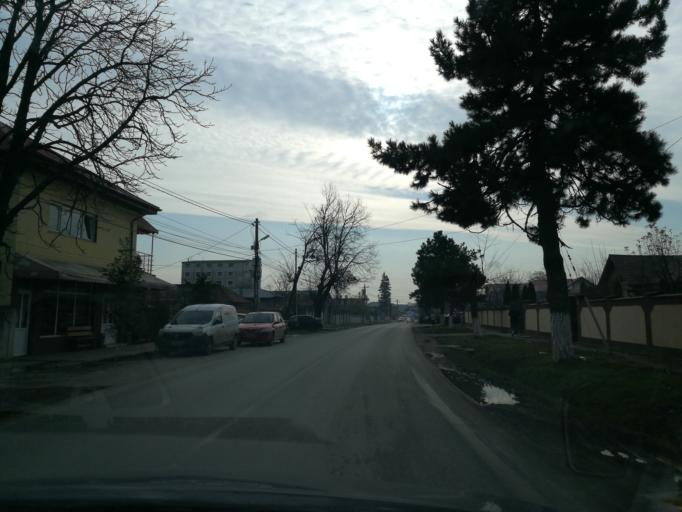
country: RO
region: Ilfov
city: Stefanestii de Jos
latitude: 44.5342
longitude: 26.2020
